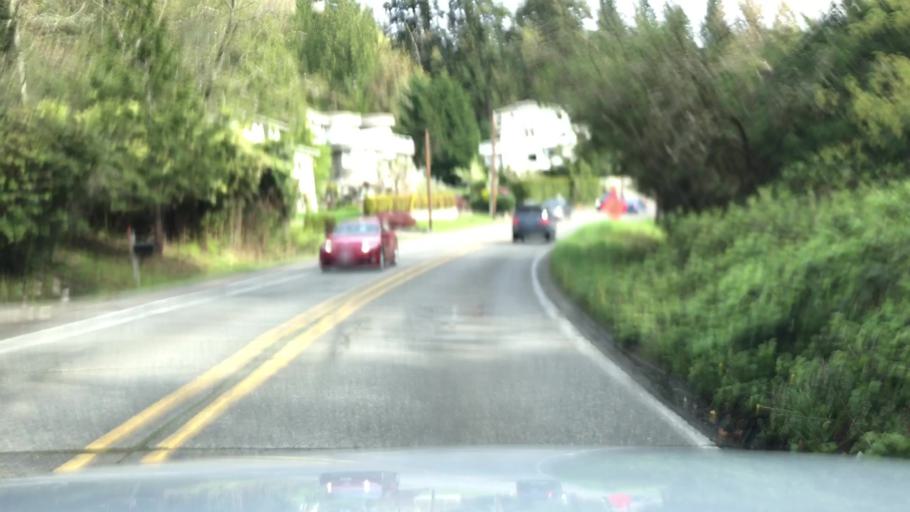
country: US
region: Washington
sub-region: King County
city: West Lake Sammamish
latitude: 47.6064
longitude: -122.1132
